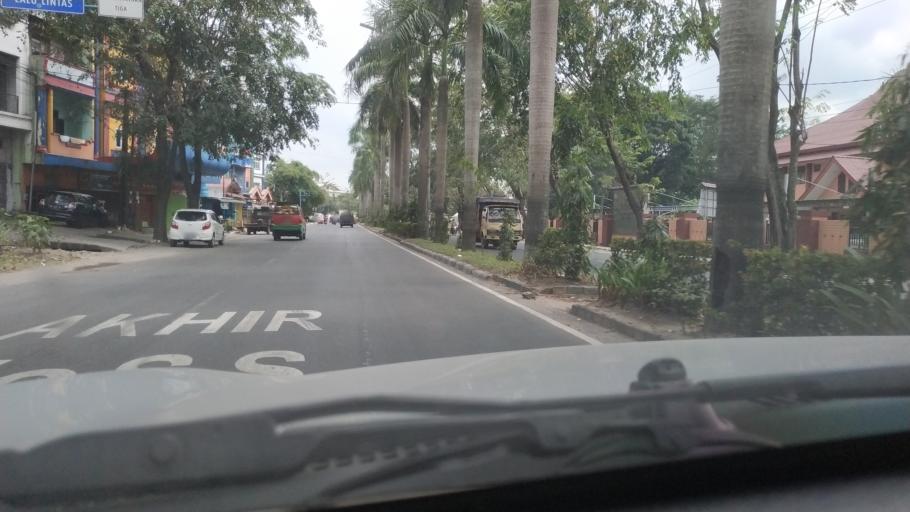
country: ID
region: North Sumatra
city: Sunggal
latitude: 3.5867
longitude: 98.6129
